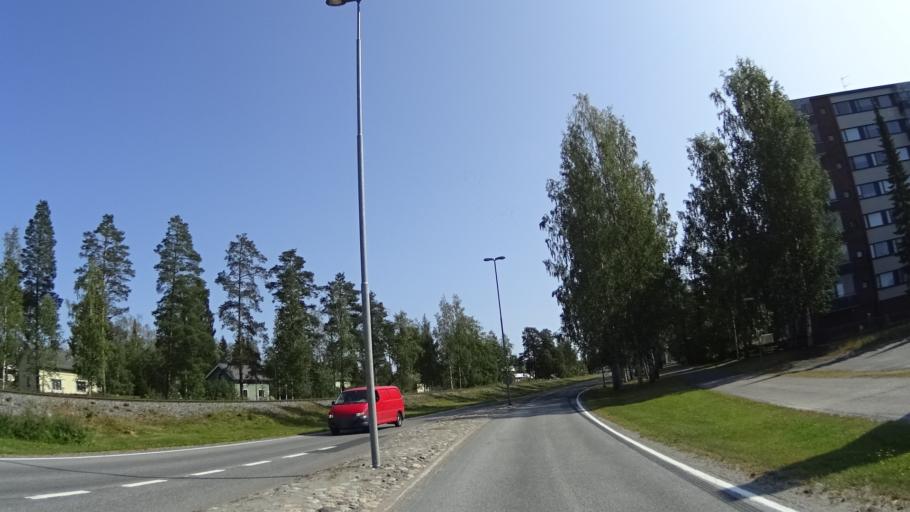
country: FI
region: Pirkanmaa
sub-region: Ylae-Pirkanmaa
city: Maenttae
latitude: 62.0299
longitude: 24.6171
